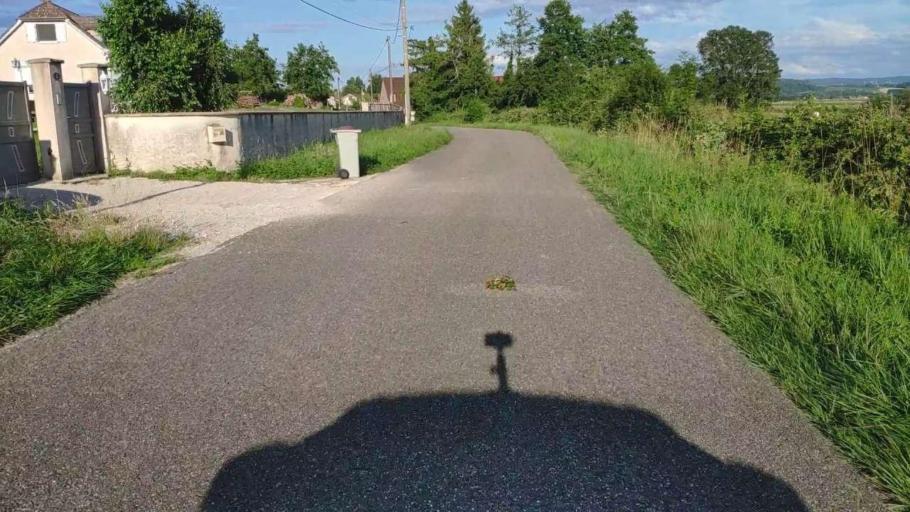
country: FR
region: Franche-Comte
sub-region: Departement du Jura
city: Bletterans
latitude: 46.7817
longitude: 5.4865
